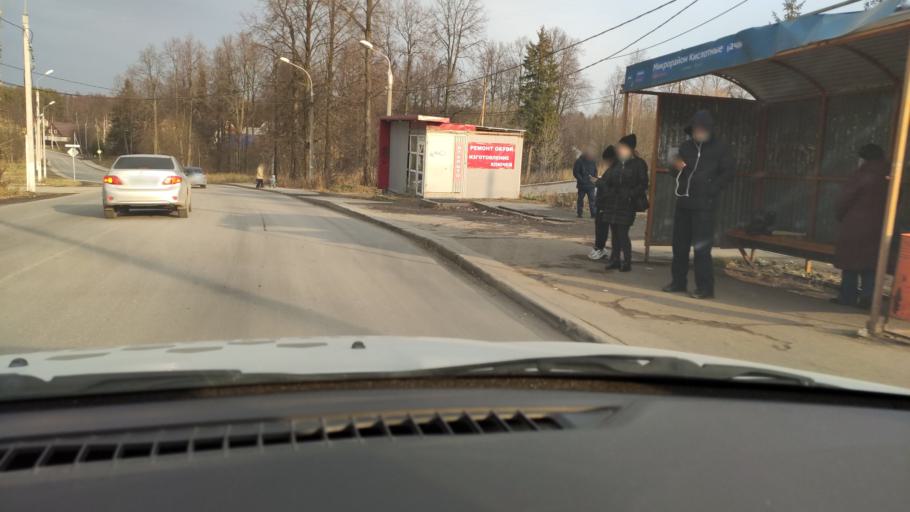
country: RU
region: Perm
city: Perm
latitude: 58.0887
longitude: 56.4016
